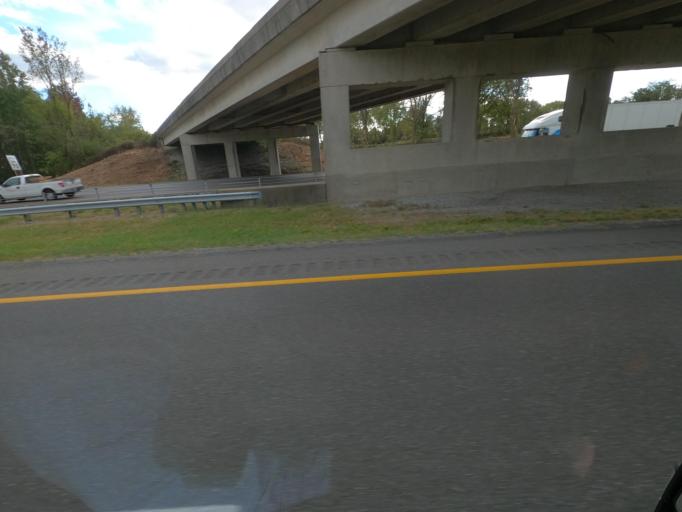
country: US
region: Kentucky
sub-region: McCracken County
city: Hendron
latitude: 37.0459
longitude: -88.6460
